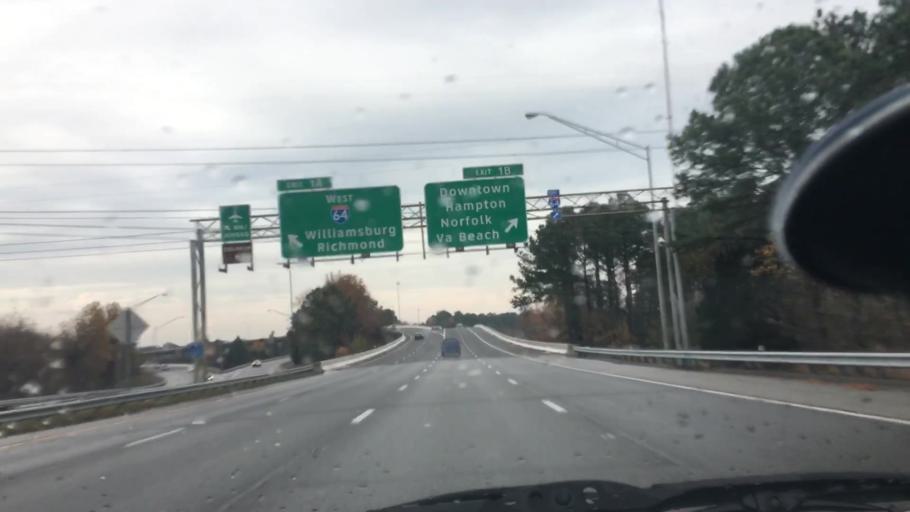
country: US
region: Virginia
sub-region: City of Hampton
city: Hampton
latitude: 37.0270
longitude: -76.3788
